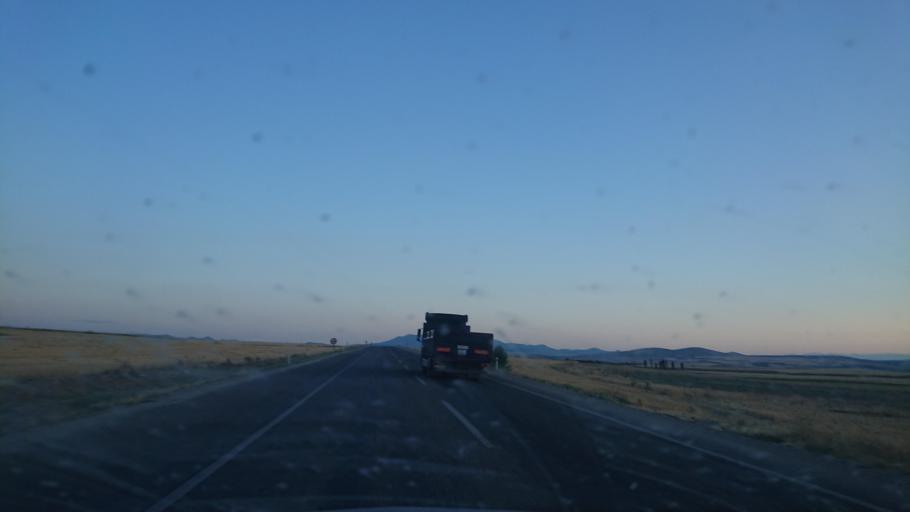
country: TR
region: Aksaray
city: Balci
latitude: 38.8419
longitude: 34.1420
